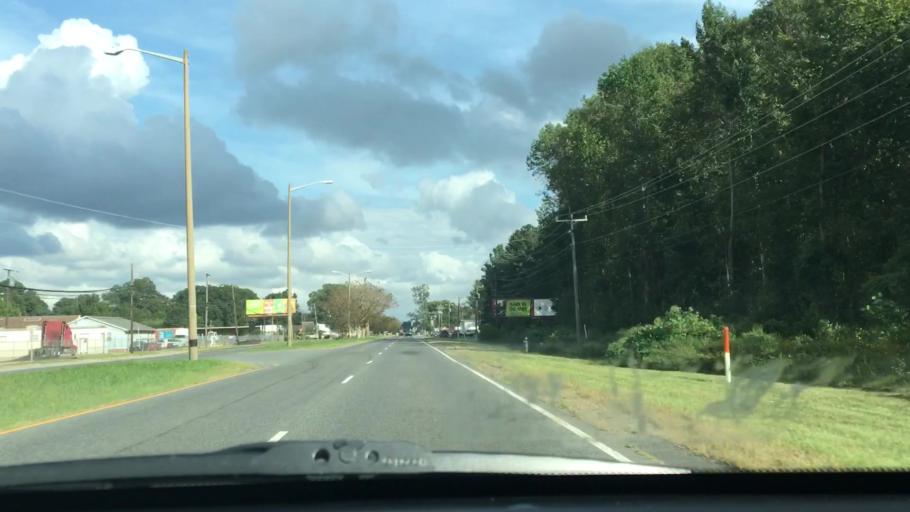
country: US
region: Virginia
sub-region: City of Portsmouth
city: Portsmouth Heights
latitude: 36.7726
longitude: -76.3317
